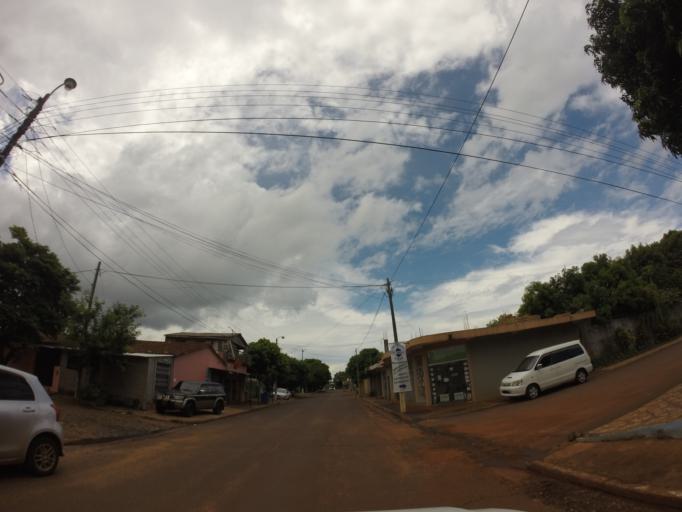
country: PY
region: Alto Parana
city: Ciudad del Este
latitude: -25.4142
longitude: -54.6283
